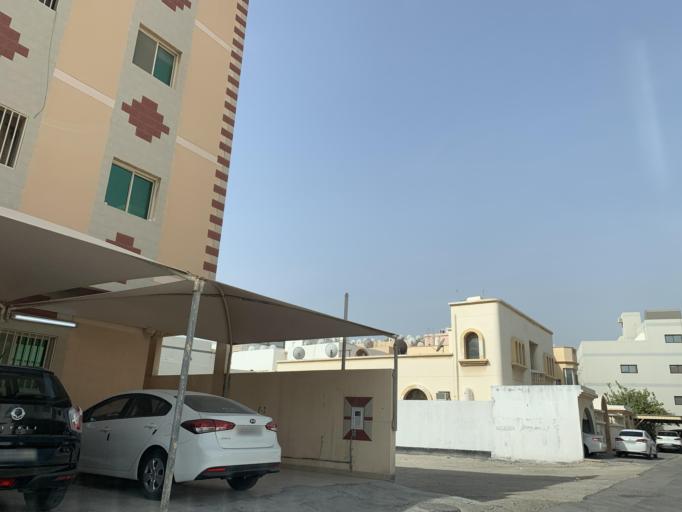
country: BH
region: Northern
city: Madinat `Isa
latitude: 26.1751
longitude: 50.5638
